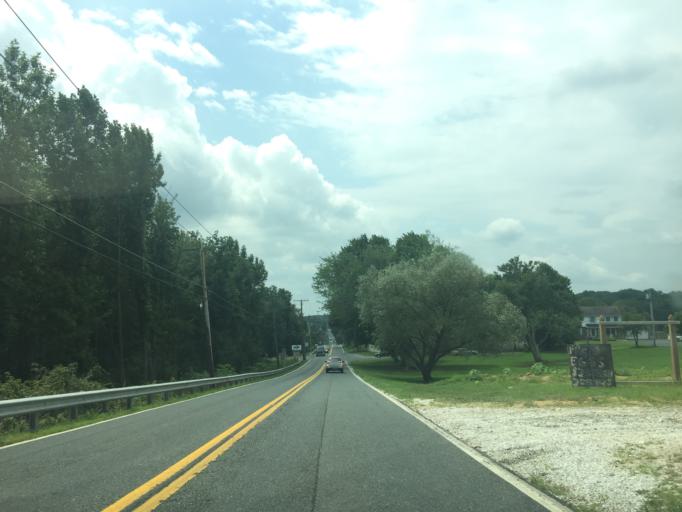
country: US
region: Maryland
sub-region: Baltimore County
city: White Marsh
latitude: 39.3928
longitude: -76.4251
